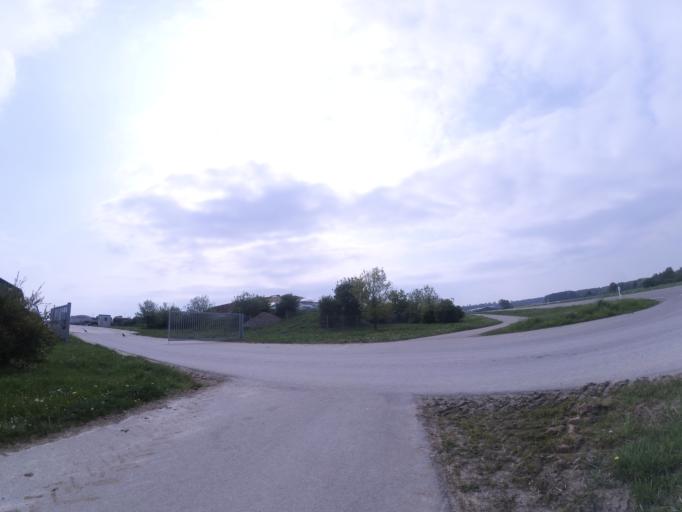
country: DE
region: Baden-Wuerttemberg
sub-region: Tuebingen Region
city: Staig
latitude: 48.3354
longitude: 9.9569
